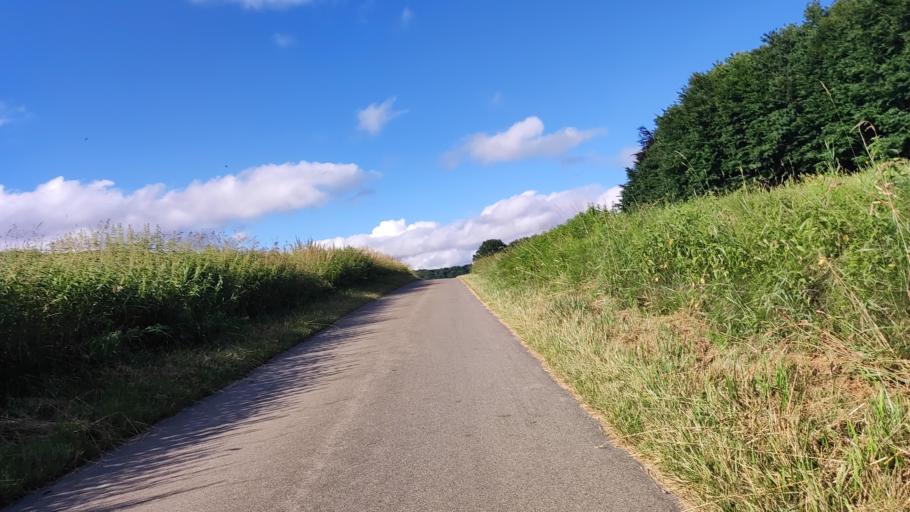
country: DE
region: Bavaria
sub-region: Swabia
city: Zusmarshausen
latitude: 48.3779
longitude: 10.5849
